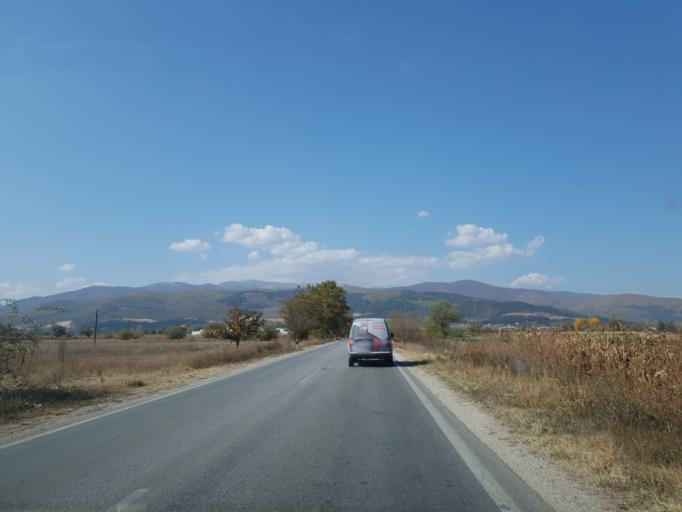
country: MK
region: Kicevo
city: Kicevo
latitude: 41.4877
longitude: 20.9724
